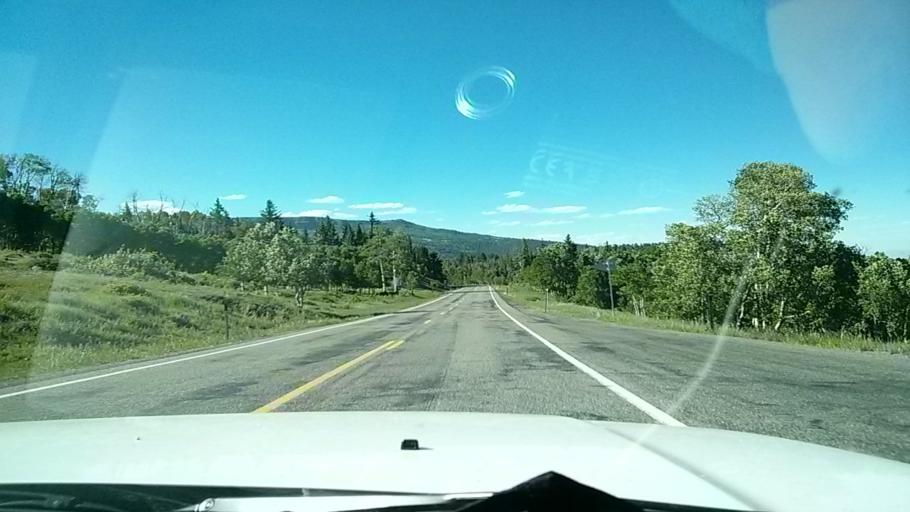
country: US
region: Utah
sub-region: Wayne County
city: Loa
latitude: 38.0723
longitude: -111.3379
